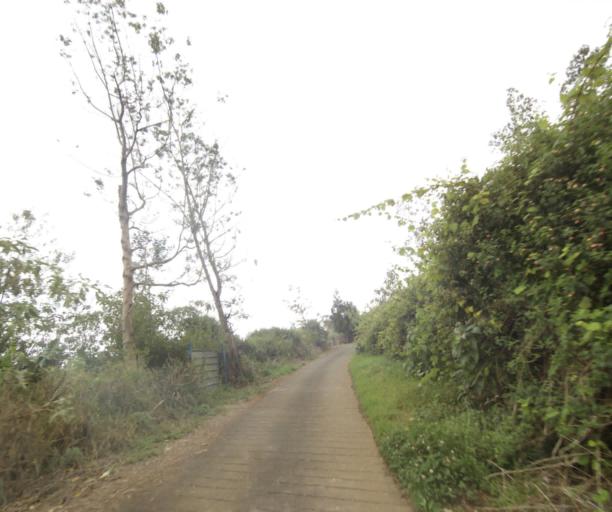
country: RE
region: Reunion
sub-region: Reunion
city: Saint-Paul
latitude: -21.0141
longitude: 55.3518
